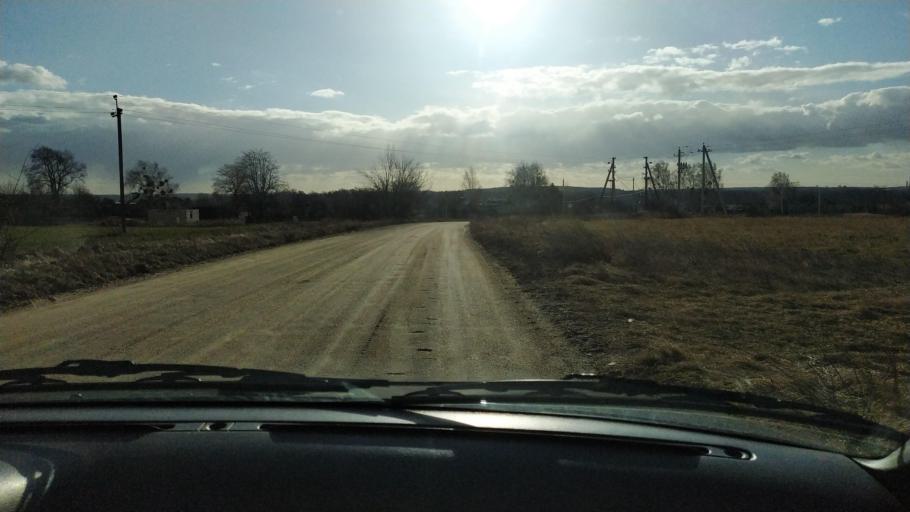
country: BY
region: Brest
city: Kamyanyets
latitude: 52.4246
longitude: 23.8217
